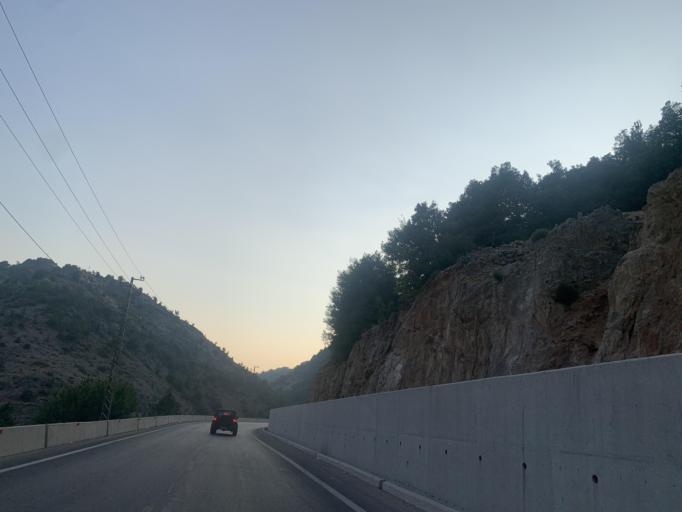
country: LB
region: Liban-Nord
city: Amioun
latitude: 34.1360
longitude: 35.8282
